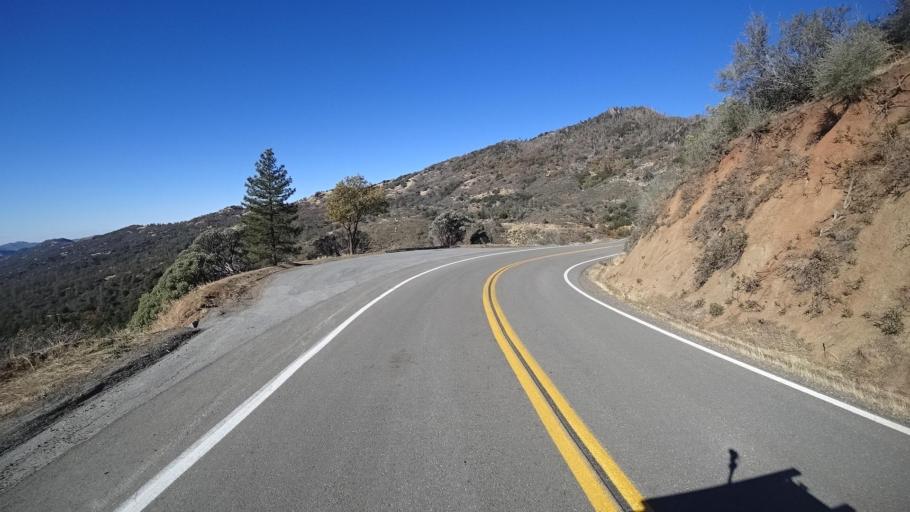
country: US
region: California
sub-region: Kern County
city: Alta Sierra
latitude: 35.7435
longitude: -118.5813
